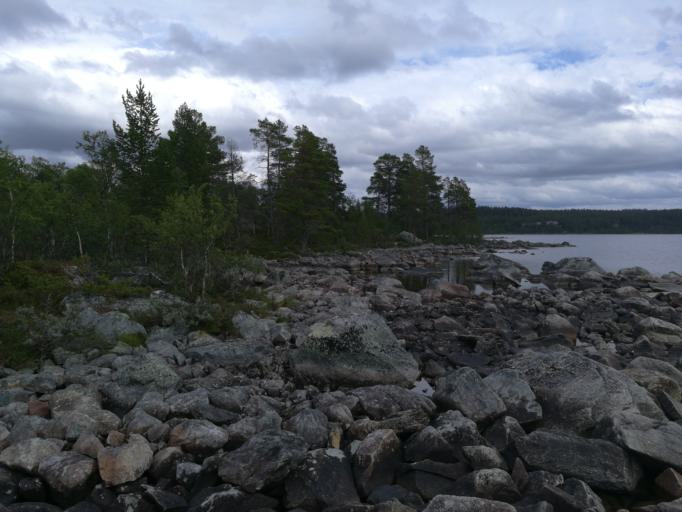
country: NO
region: Sor-Trondelag
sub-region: Roros
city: Roros
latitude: 62.4095
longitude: 11.9547
